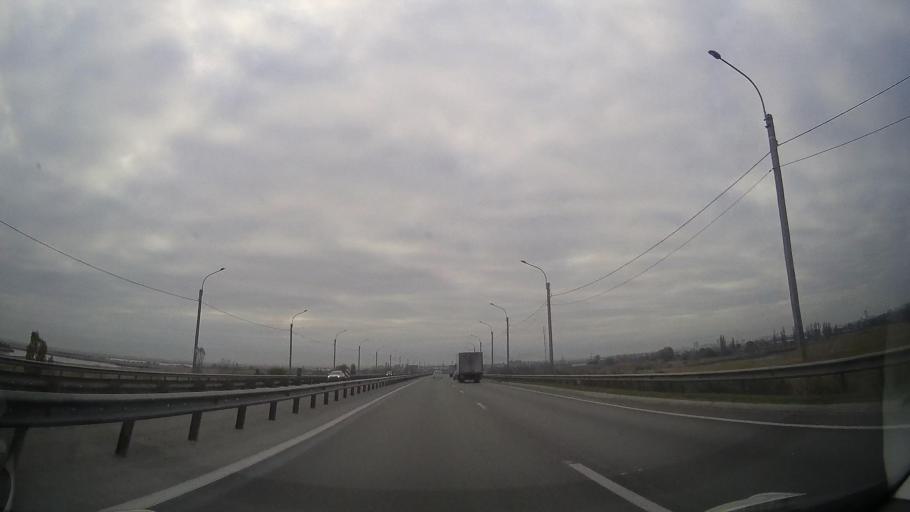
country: RU
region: Rostov
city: Bataysk
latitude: 47.1637
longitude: 39.7595
